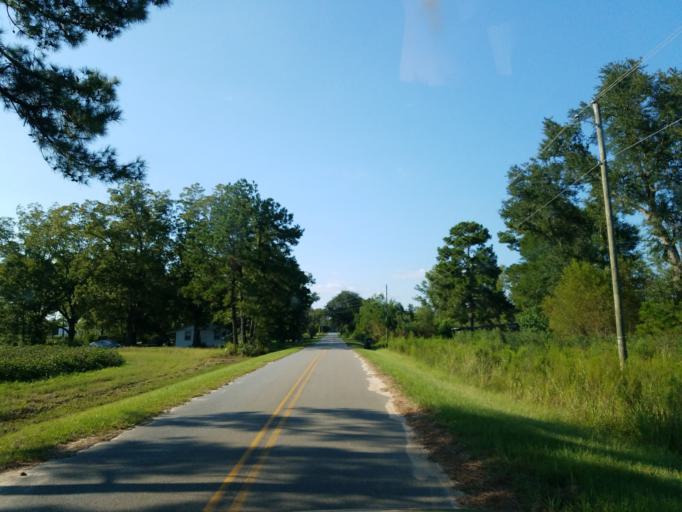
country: US
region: Georgia
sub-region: Lowndes County
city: Hahira
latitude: 31.0405
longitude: -83.3924
